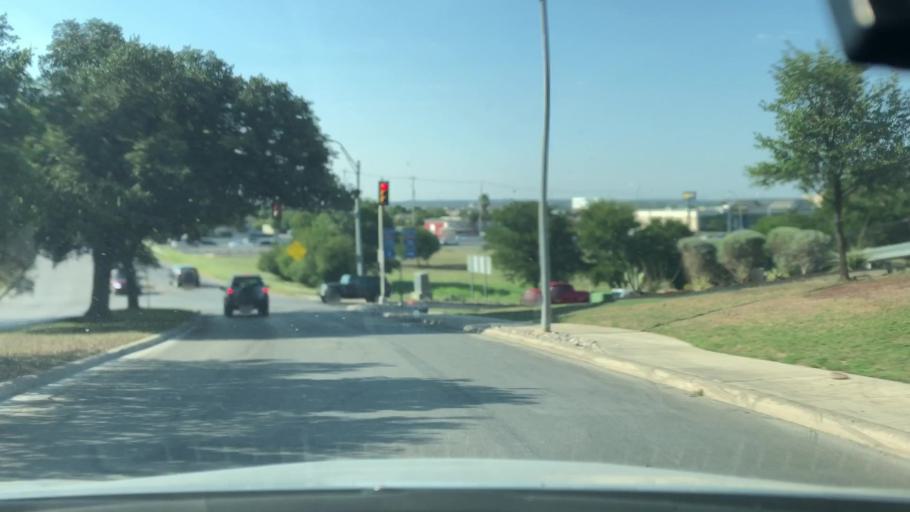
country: US
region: Texas
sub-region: Bexar County
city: Selma
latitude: 29.5758
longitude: -98.3204
